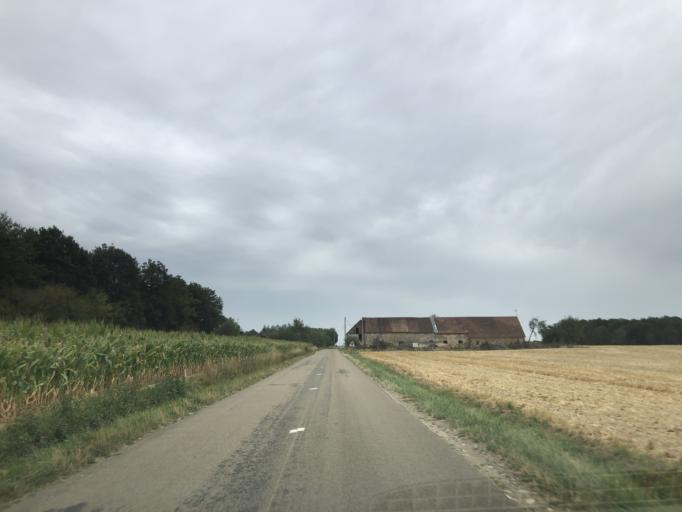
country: FR
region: Centre
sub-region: Departement du Loiret
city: Courtenay
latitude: 47.9873
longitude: 3.1429
